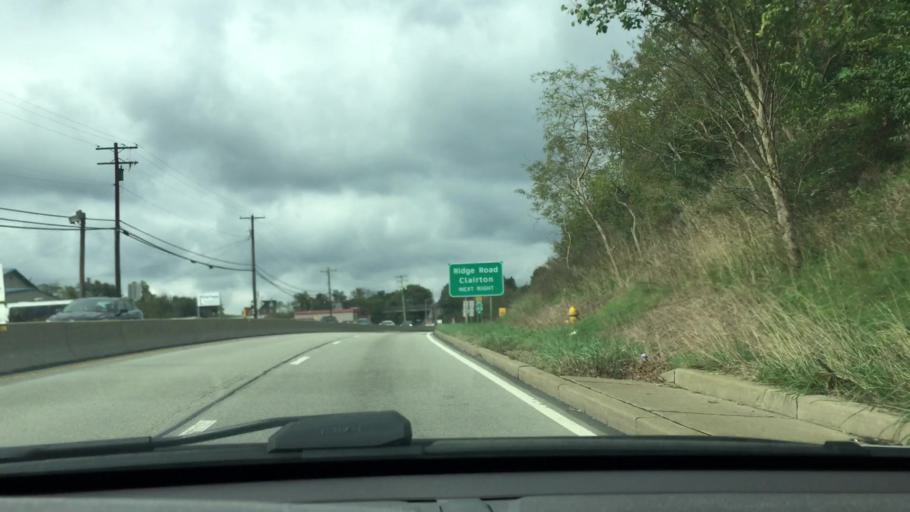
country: US
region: Pennsylvania
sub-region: Allegheny County
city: Elizabeth
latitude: 40.2768
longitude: -79.9044
